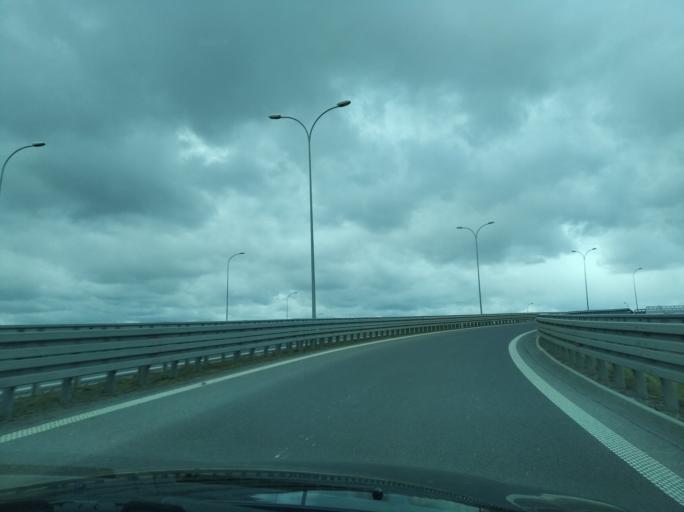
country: PL
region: Subcarpathian Voivodeship
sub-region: Powiat lancucki
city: Lancut
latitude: 50.0982
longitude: 22.2249
